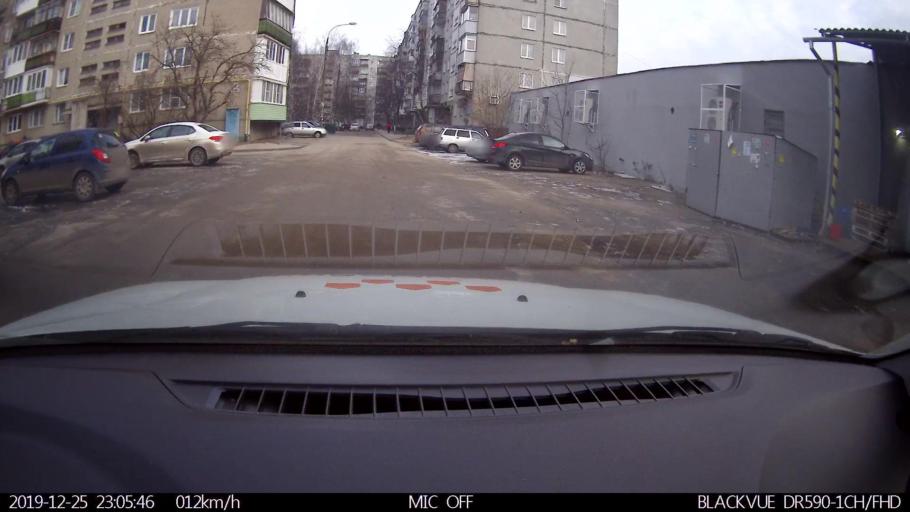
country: RU
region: Nizjnij Novgorod
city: Gorbatovka
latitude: 56.3612
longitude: 43.8062
